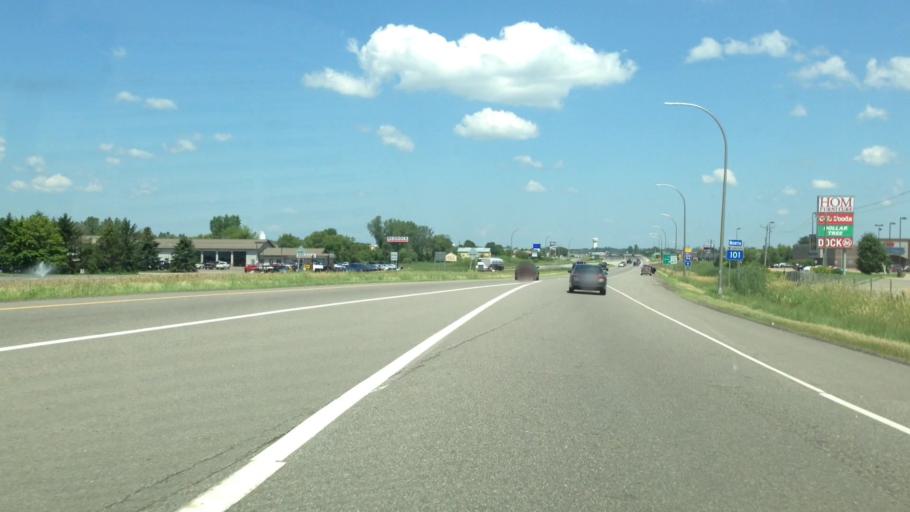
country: US
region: Minnesota
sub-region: Hennepin County
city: Rogers
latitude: 45.2031
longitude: -93.5530
